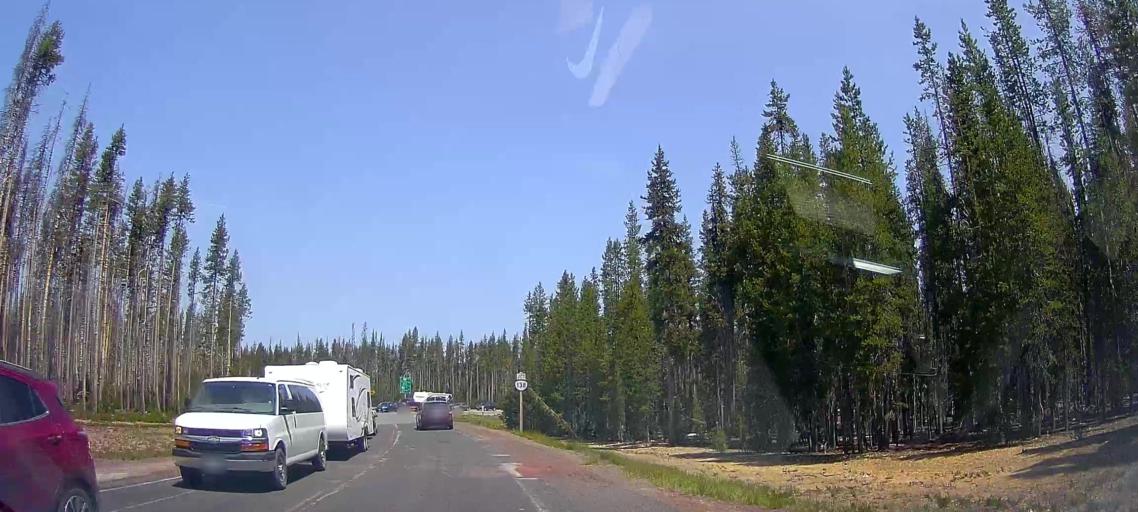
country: US
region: Oregon
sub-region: Lane County
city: Oakridge
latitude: 43.0877
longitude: -122.1163
